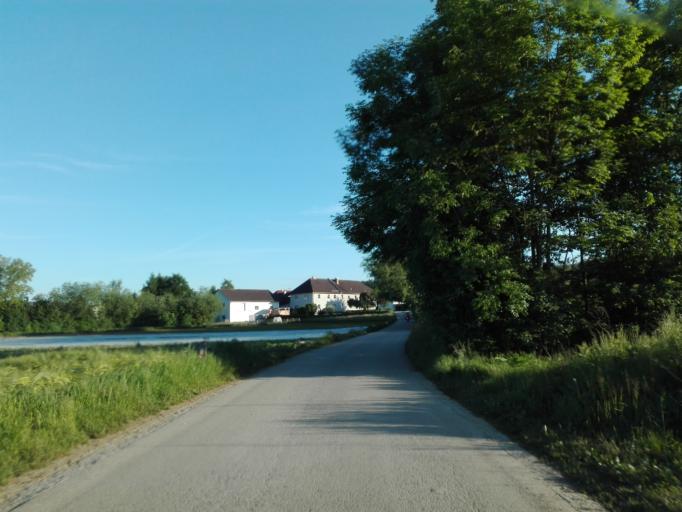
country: AT
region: Upper Austria
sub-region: Politischer Bezirk Urfahr-Umgebung
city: Feldkirchen an der Donau
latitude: 48.3258
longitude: 14.0003
